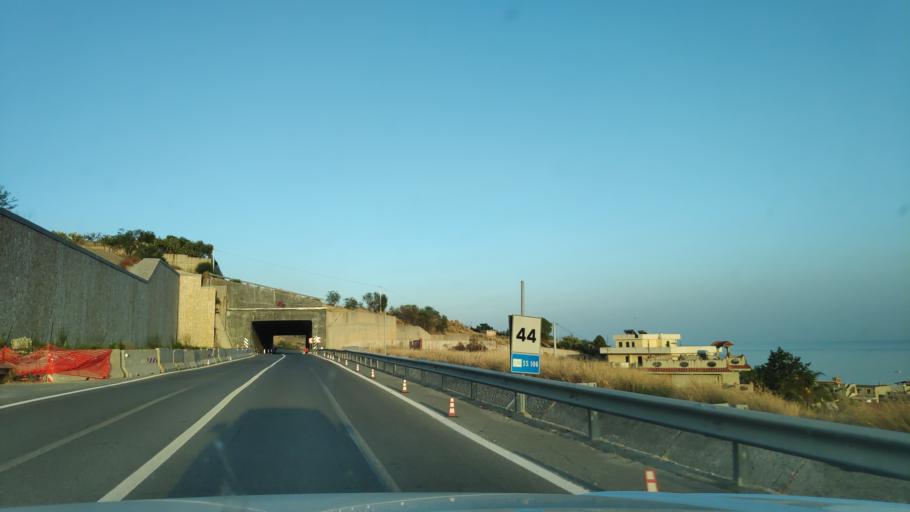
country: IT
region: Calabria
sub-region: Provincia di Reggio Calabria
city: Bova Marina
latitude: 37.9347
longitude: 15.9190
